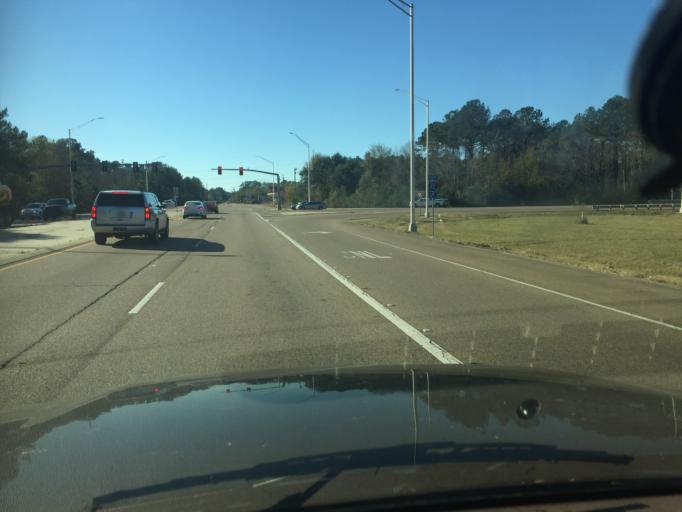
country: US
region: Louisiana
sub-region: Saint Tammany Parish
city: Slidell
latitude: 30.3090
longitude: -89.7713
